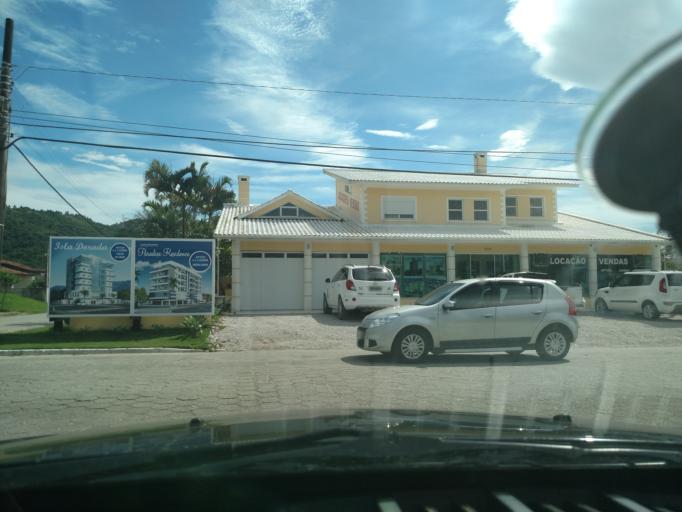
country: BR
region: Santa Catarina
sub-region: Tijucas
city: Tijucas
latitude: -27.3230
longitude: -48.5436
